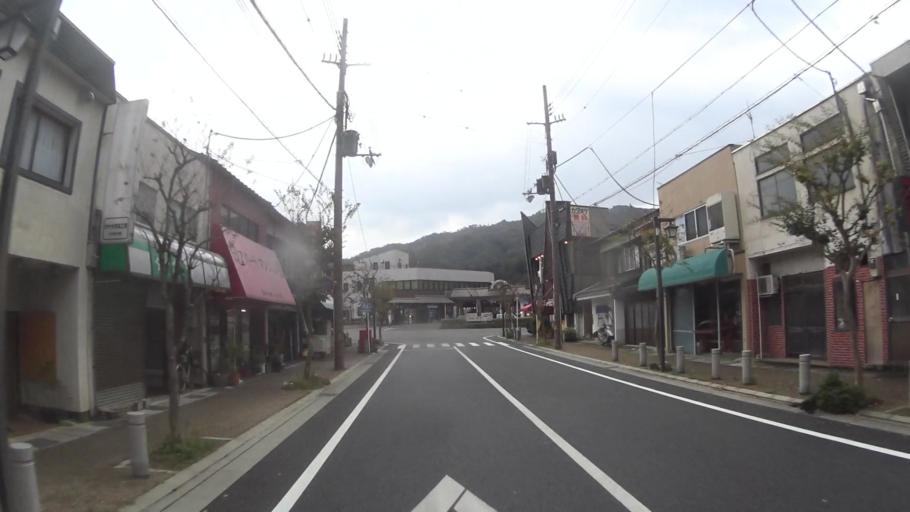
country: JP
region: Kyoto
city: Miyazu
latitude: 35.5349
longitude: 135.1987
